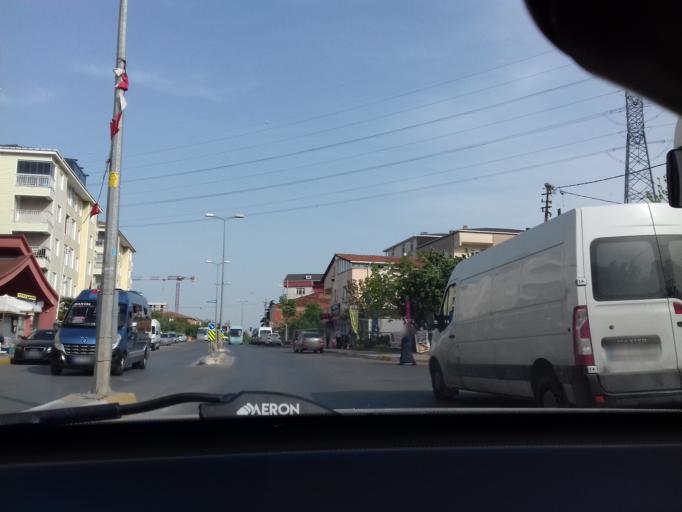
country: TR
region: Istanbul
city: Pendik
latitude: 40.9066
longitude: 29.2618
